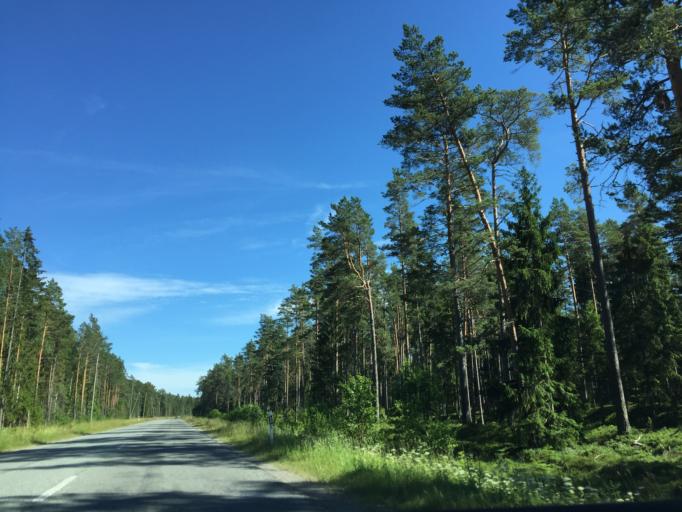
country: LV
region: Rojas
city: Roja
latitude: 57.4910
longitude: 22.8350
